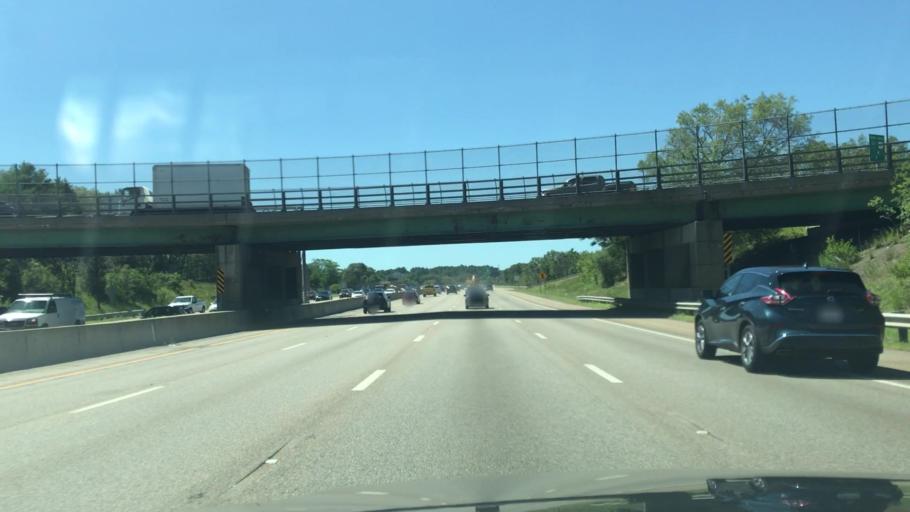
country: US
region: Massachusetts
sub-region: Norfolk County
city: Dedham
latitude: 42.2236
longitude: -71.1715
